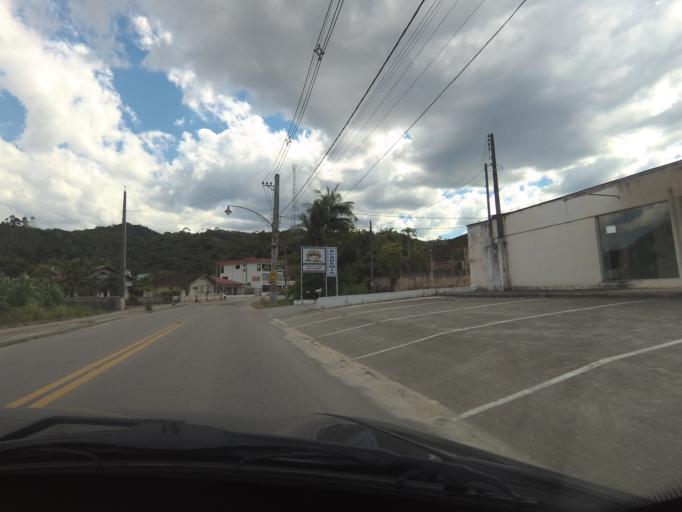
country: BR
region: Santa Catarina
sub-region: Brusque
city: Brusque
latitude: -27.0740
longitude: -48.9330
